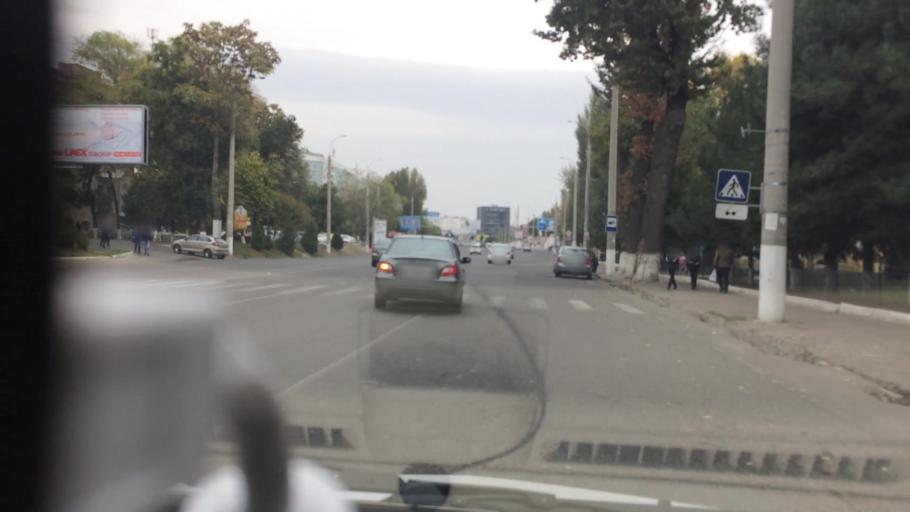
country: UZ
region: Toshkent
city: Salor
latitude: 41.3180
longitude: 69.3138
